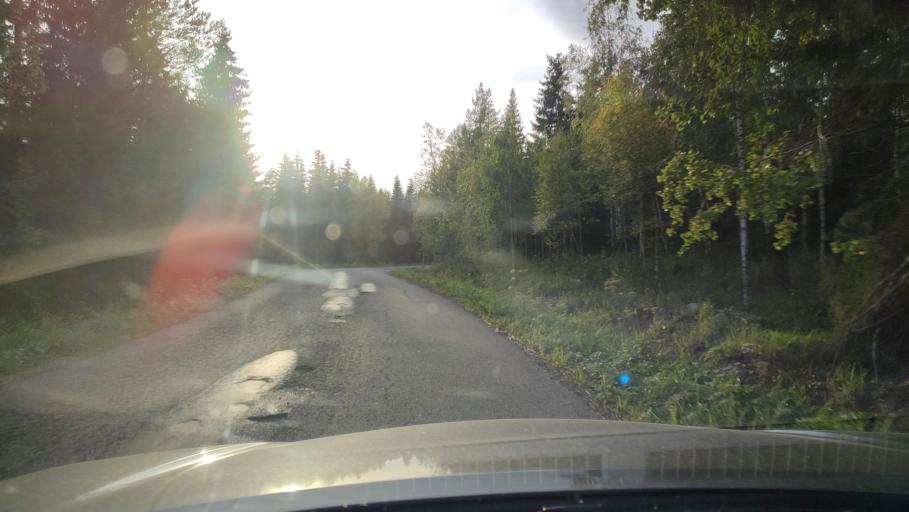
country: FI
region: Ostrobothnia
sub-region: Sydosterbotten
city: Kristinestad
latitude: 62.1530
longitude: 21.5345
